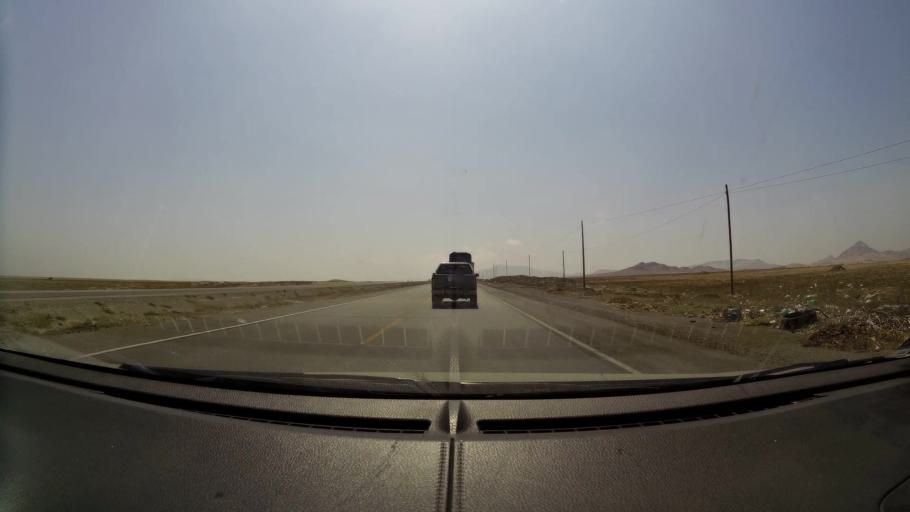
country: PE
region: Lambayeque
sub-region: Provincia de Chiclayo
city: Mocupe
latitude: -6.9654
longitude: -79.6829
